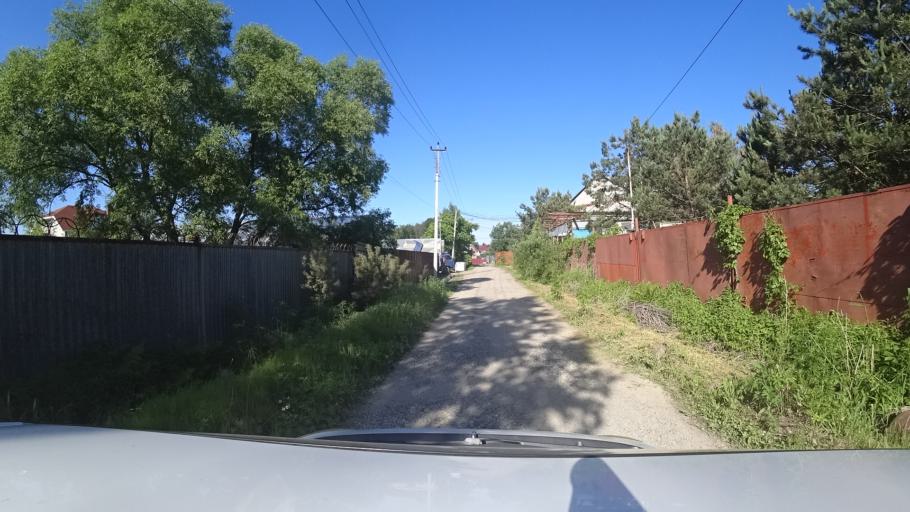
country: RU
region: Khabarovsk Krai
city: Topolevo
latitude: 48.5406
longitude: 135.1780
